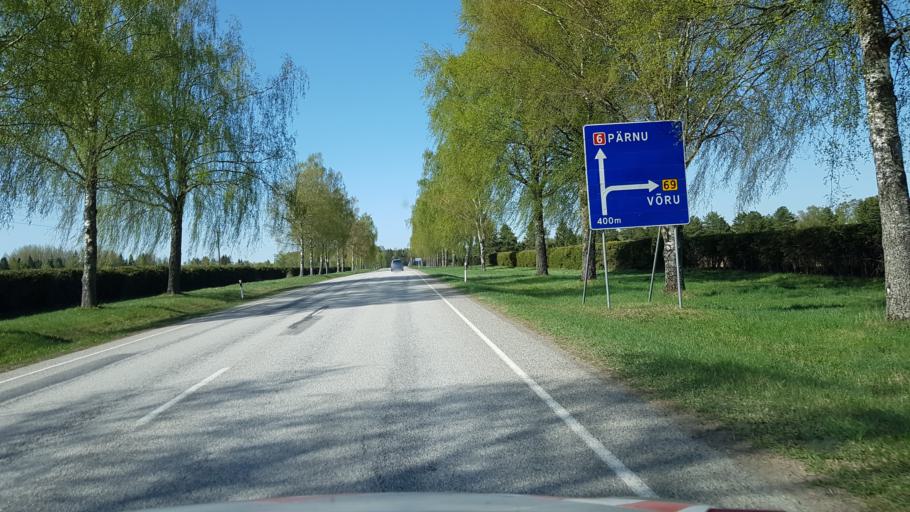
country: EE
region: Valgamaa
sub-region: Torva linn
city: Torva
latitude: 57.9745
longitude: 25.9558
